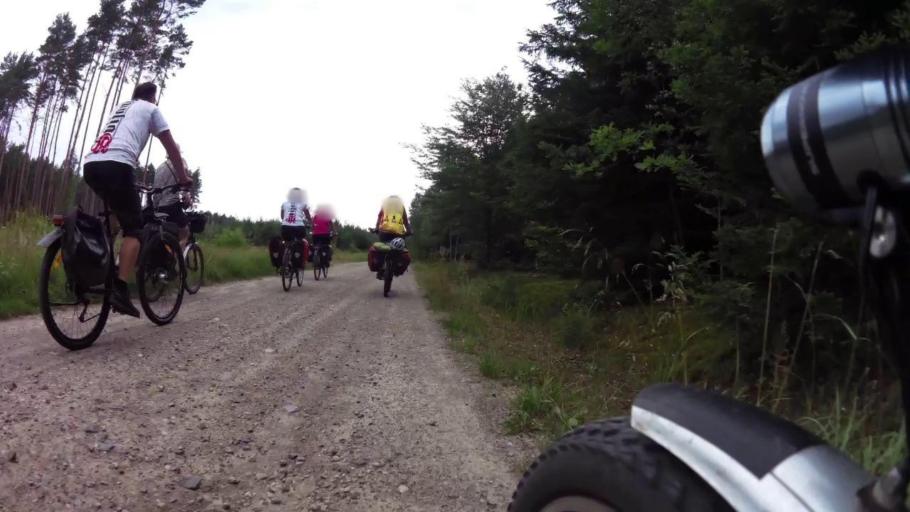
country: PL
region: West Pomeranian Voivodeship
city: Trzcinsko Zdroj
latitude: 52.8509
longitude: 14.6017
